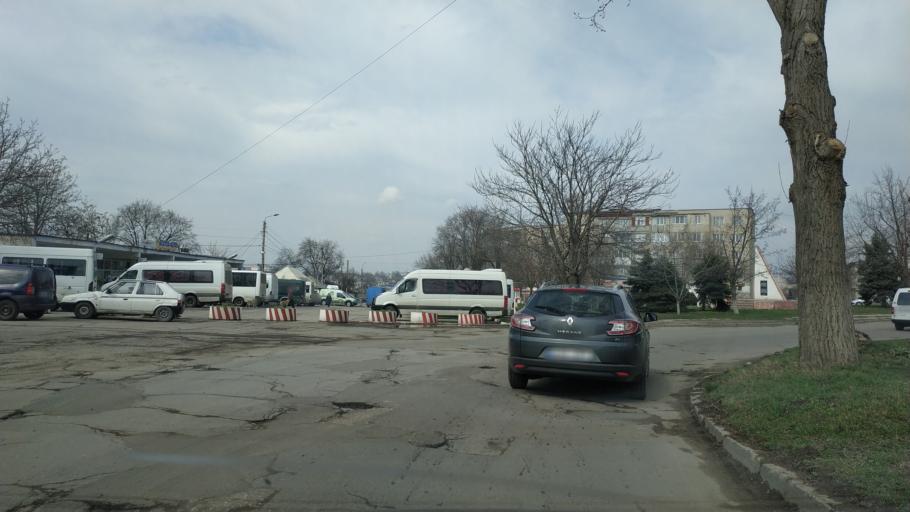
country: MD
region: Cahul
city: Cahul
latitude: 45.8949
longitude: 28.1997
